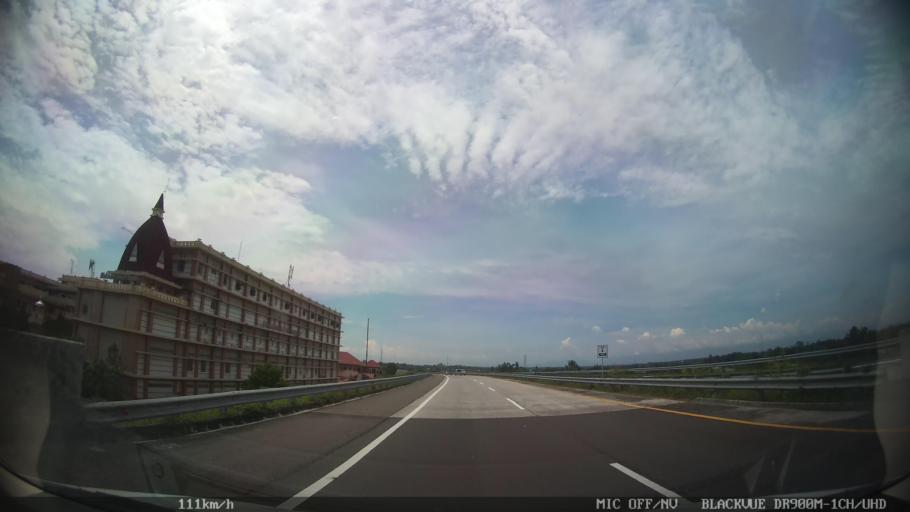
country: ID
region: North Sumatra
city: Percut
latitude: 3.5529
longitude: 98.8525
